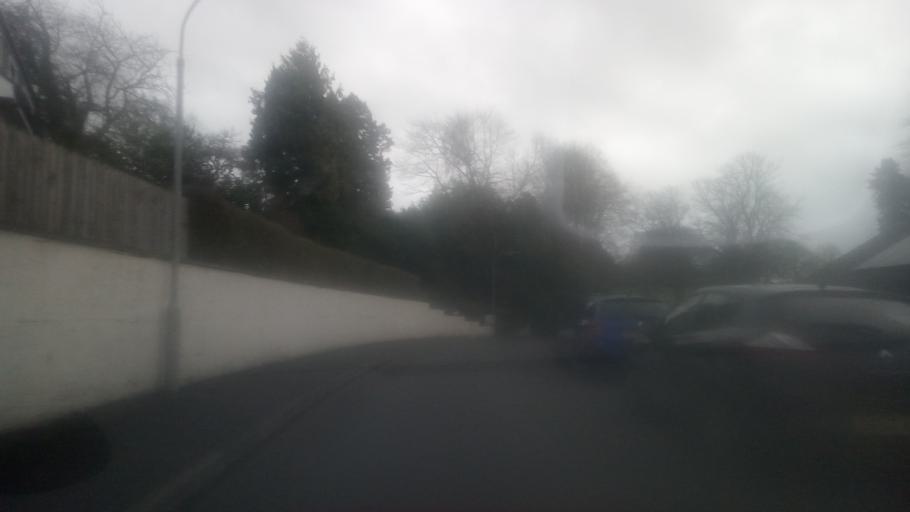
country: GB
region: Scotland
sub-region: The Scottish Borders
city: Jedburgh
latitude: 55.4749
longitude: -2.5509
